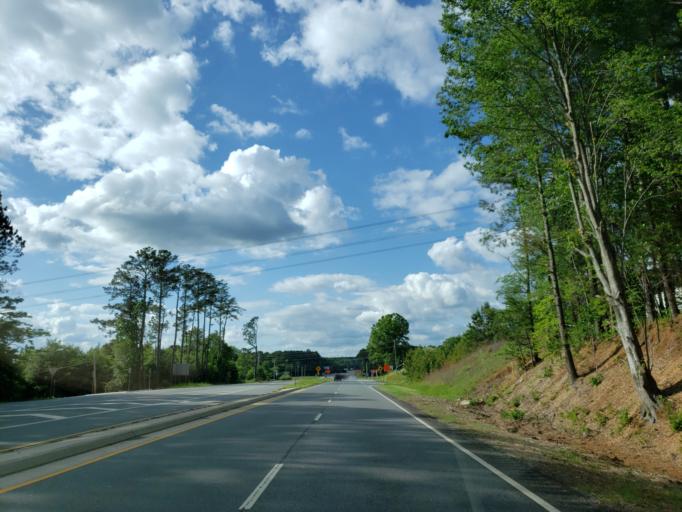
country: US
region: Georgia
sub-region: Bartow County
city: Cartersville
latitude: 34.2277
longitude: -84.8544
